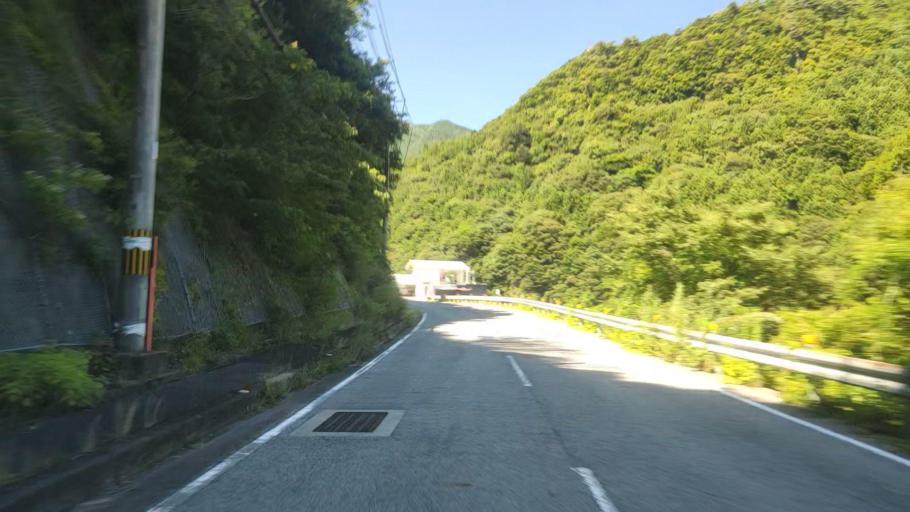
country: JP
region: Nara
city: Yoshino-cho
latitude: 34.3212
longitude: 135.9707
